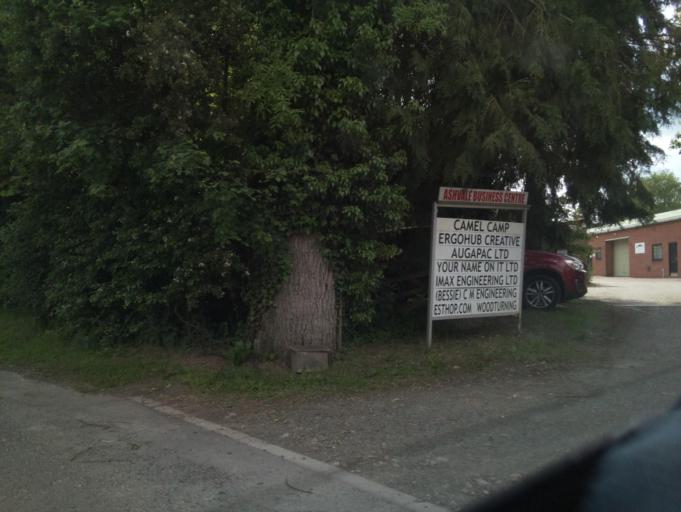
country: GB
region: England
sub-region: Herefordshire
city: Evesbatch
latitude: 52.1160
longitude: -2.4061
